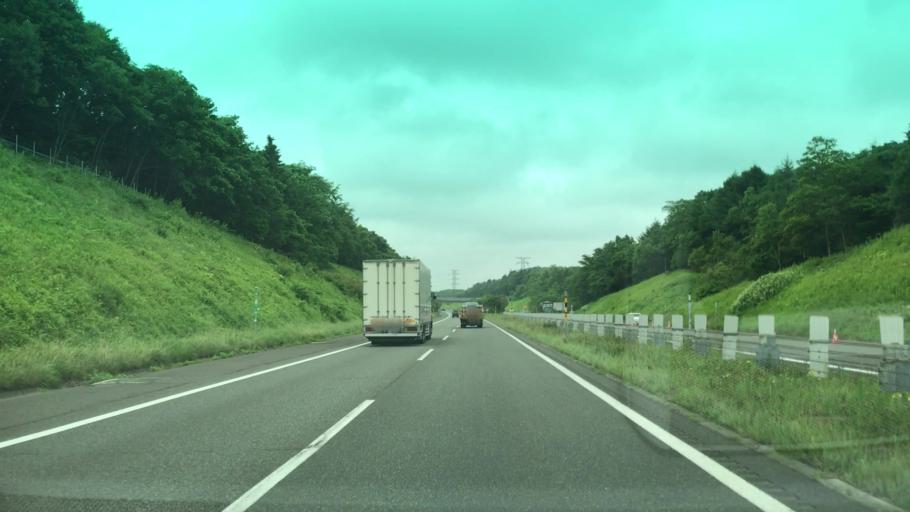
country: JP
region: Hokkaido
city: Chitose
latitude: 42.7271
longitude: 141.6530
